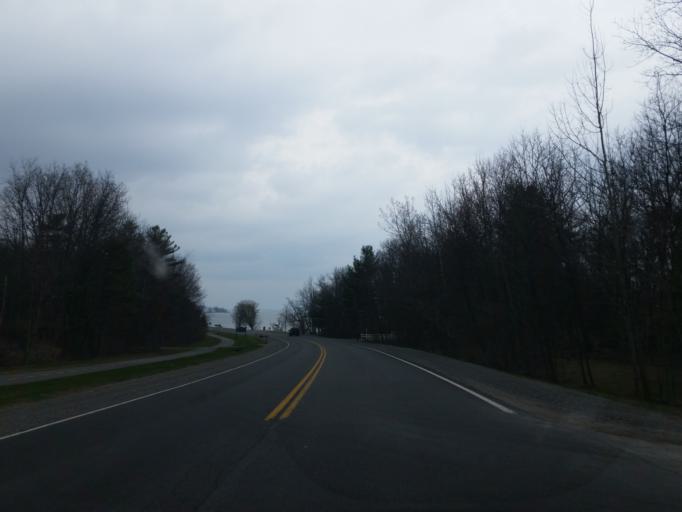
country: US
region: New York
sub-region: Jefferson County
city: Alexandria Bay
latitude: 44.4363
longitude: -75.8785
